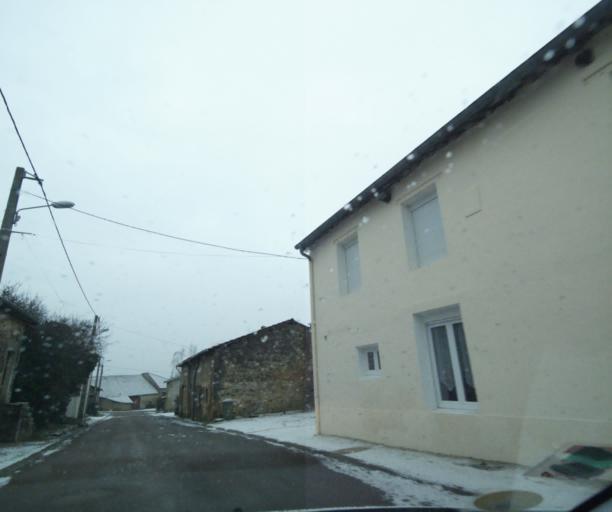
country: FR
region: Champagne-Ardenne
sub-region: Departement de la Haute-Marne
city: Wassy
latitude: 48.4605
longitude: 5.0304
